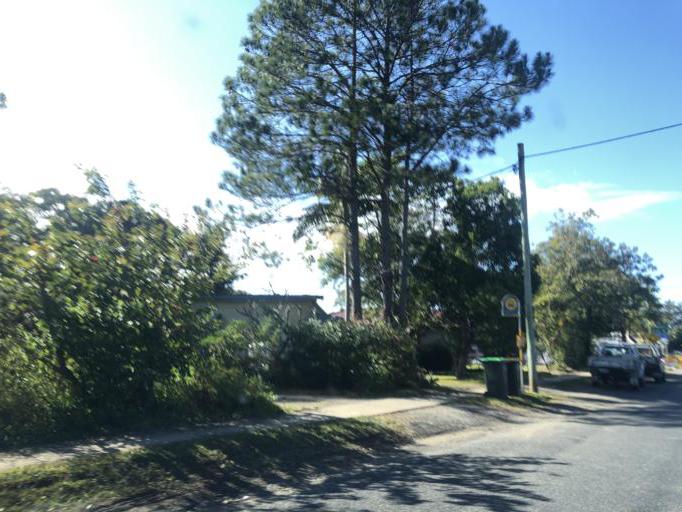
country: AU
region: New South Wales
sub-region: Coffs Harbour
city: Toormina
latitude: -30.3505
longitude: 153.0891
